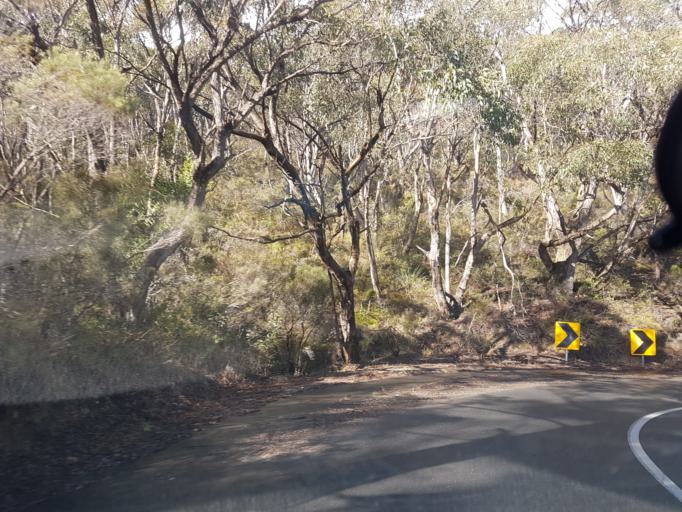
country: AU
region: South Australia
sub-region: Adelaide Hills
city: Heathfield
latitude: -35.0330
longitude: 138.7145
